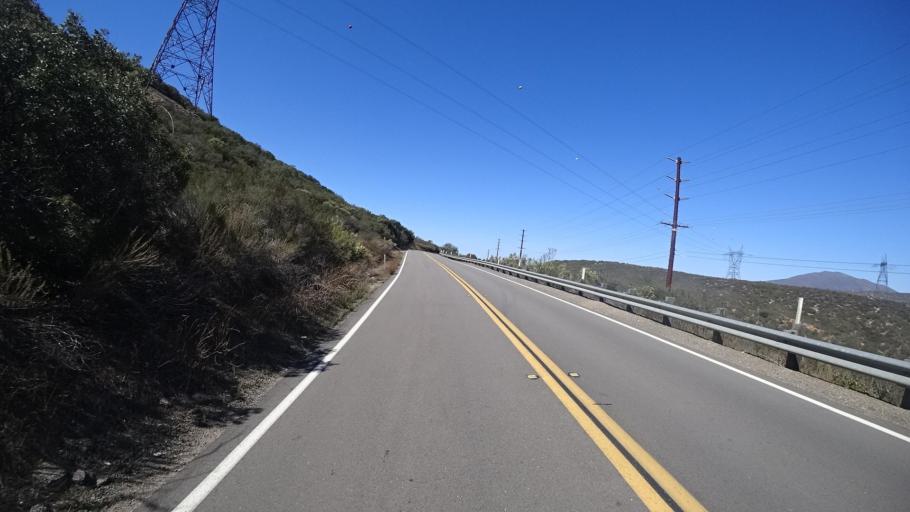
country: US
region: California
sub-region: San Diego County
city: Alpine
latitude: 32.7771
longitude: -116.7129
